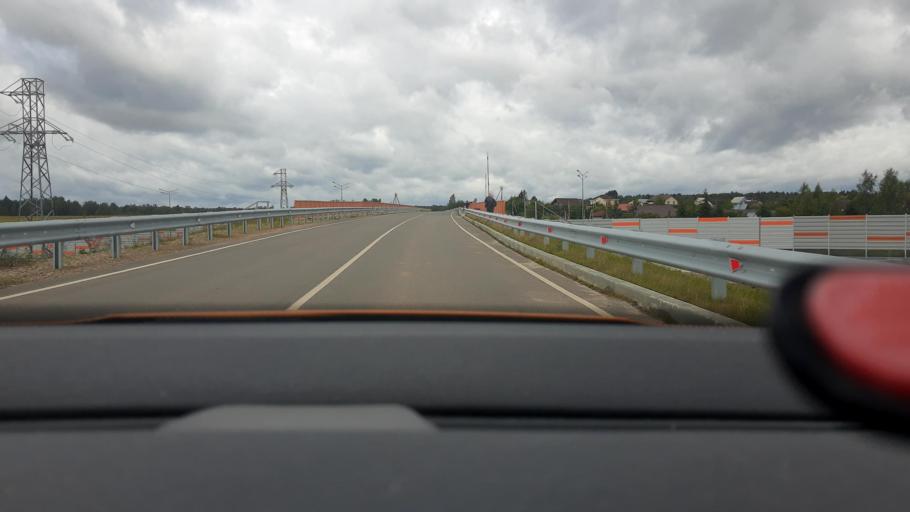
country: RU
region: Moskovskaya
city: Krasnoarmeysk
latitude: 56.0817
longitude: 38.0333
